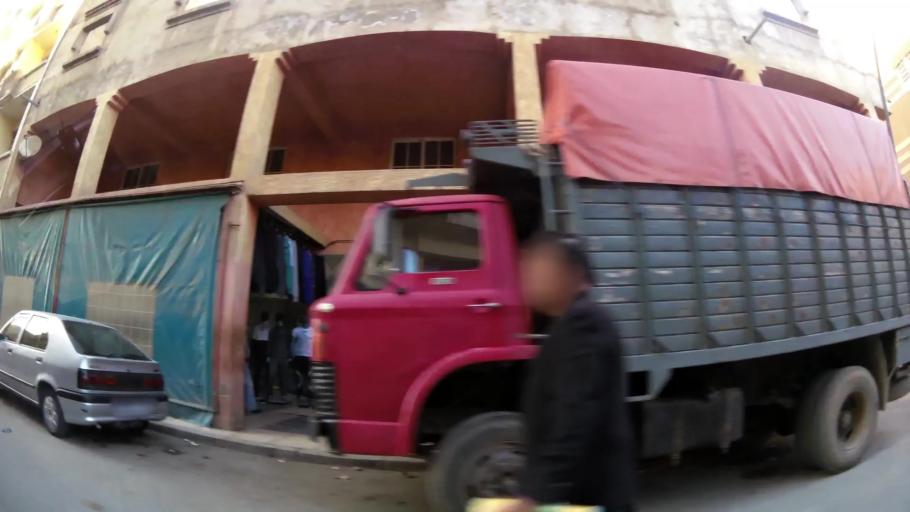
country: MA
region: Oriental
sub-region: Berkane-Taourirt
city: Berkane
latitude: 34.9228
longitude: -2.3355
